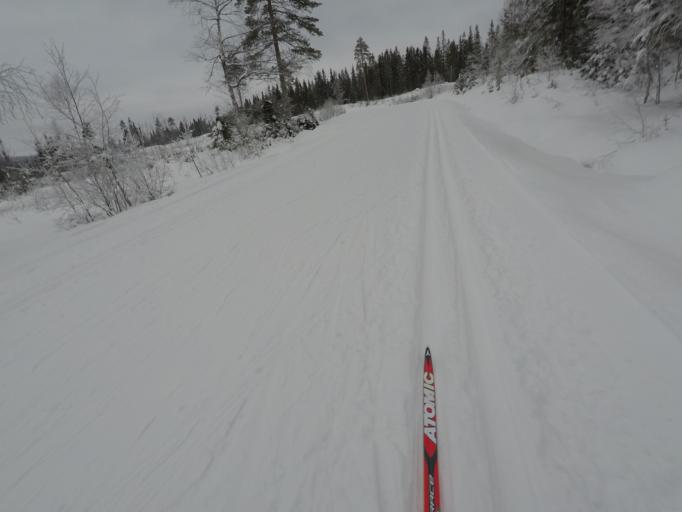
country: SE
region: Dalarna
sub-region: Ludvika Kommun
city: Abborrberget
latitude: 60.1480
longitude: 14.4886
